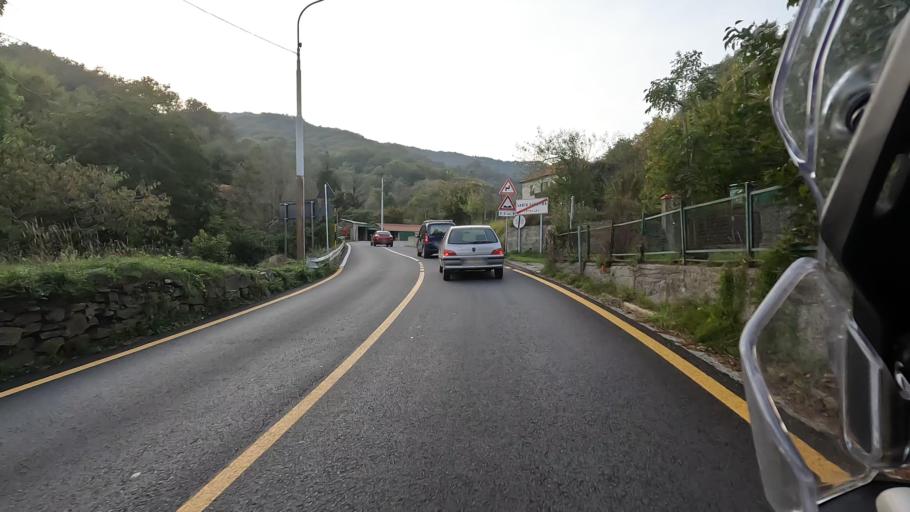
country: IT
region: Liguria
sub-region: Provincia di Savona
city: Osteria dei Cacciatori-Stella
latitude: 44.4186
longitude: 8.4792
